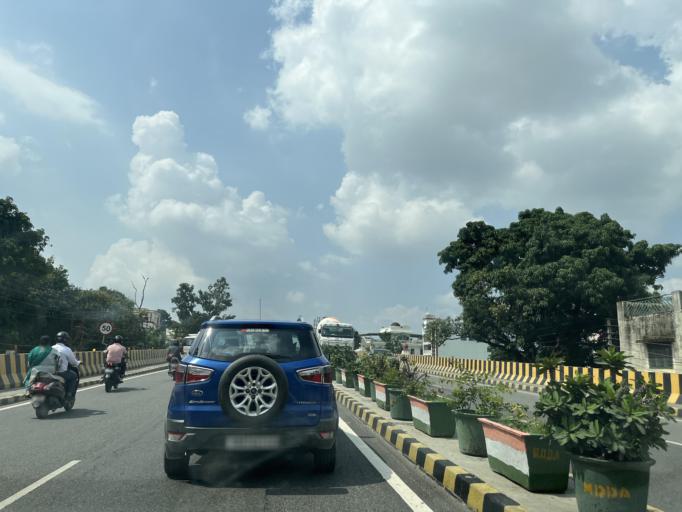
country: IN
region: Uttarakhand
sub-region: Dehradun
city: Raipur
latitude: 30.2747
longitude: 78.0763
